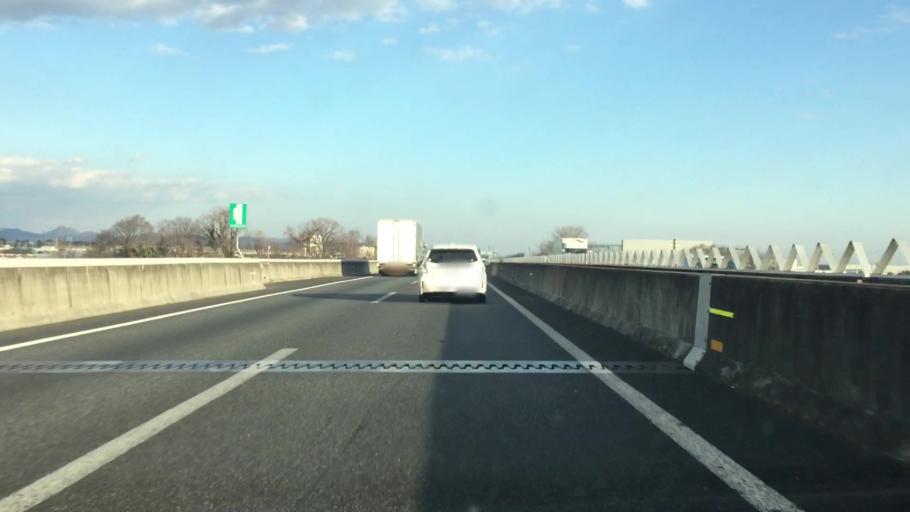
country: JP
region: Gunma
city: Isesaki
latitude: 36.3559
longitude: 139.2104
